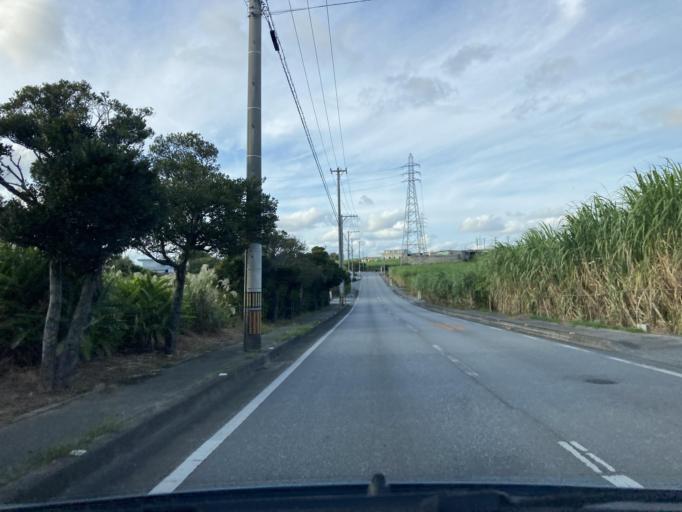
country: JP
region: Okinawa
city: Tomigusuku
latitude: 26.1552
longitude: 127.7409
